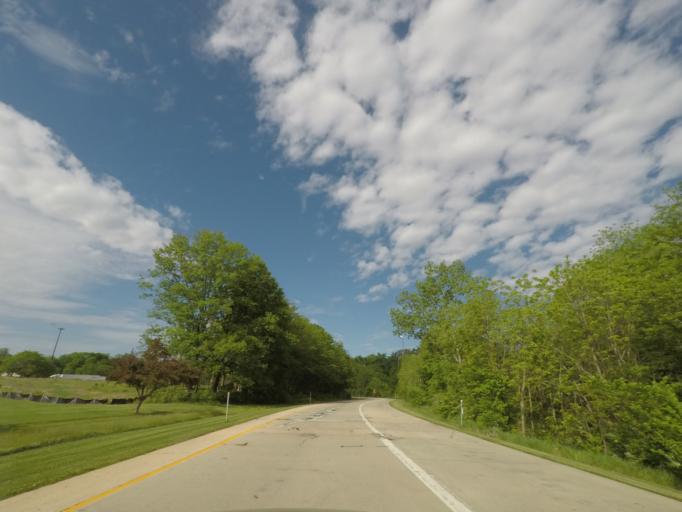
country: US
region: Illinois
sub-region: McLean County
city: Twin Grove
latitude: 40.3621
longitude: -89.1087
